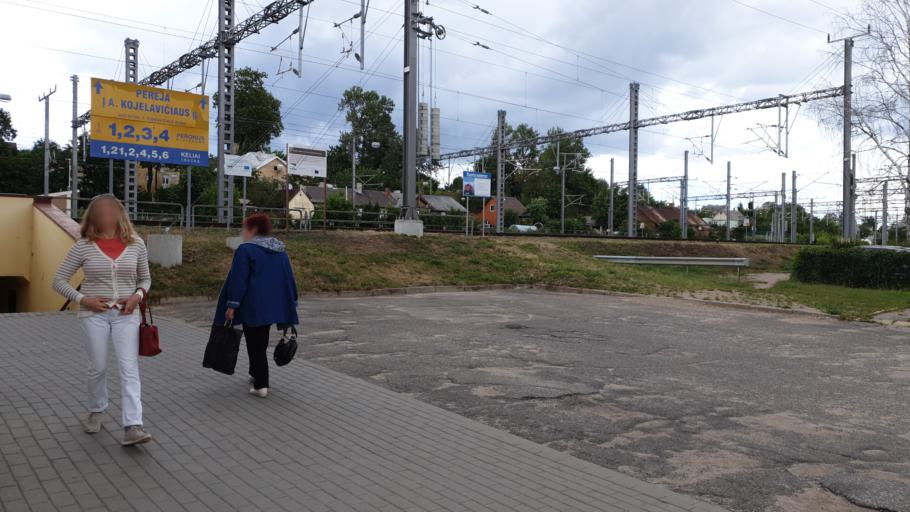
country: LT
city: Skaidiskes
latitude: 54.6937
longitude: 25.4093
